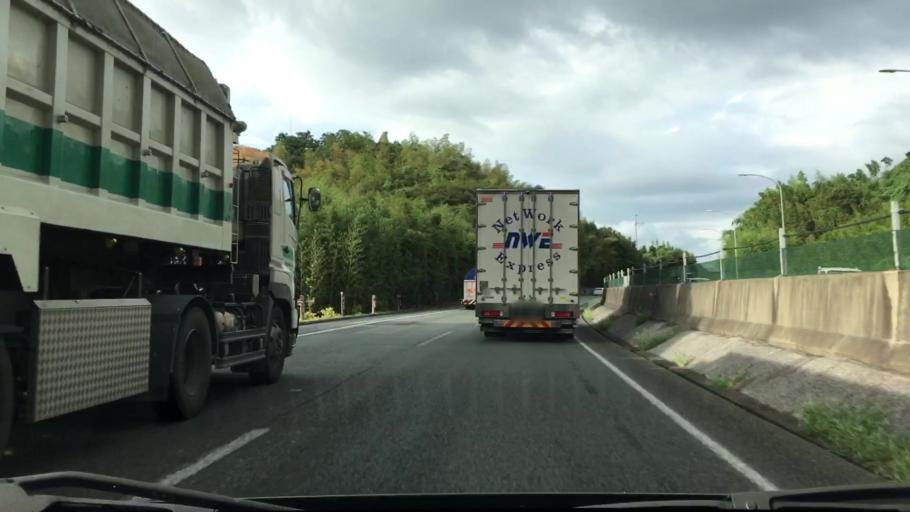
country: JP
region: Fukuoka
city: Nishifukuma
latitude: 33.7469
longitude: 130.5280
